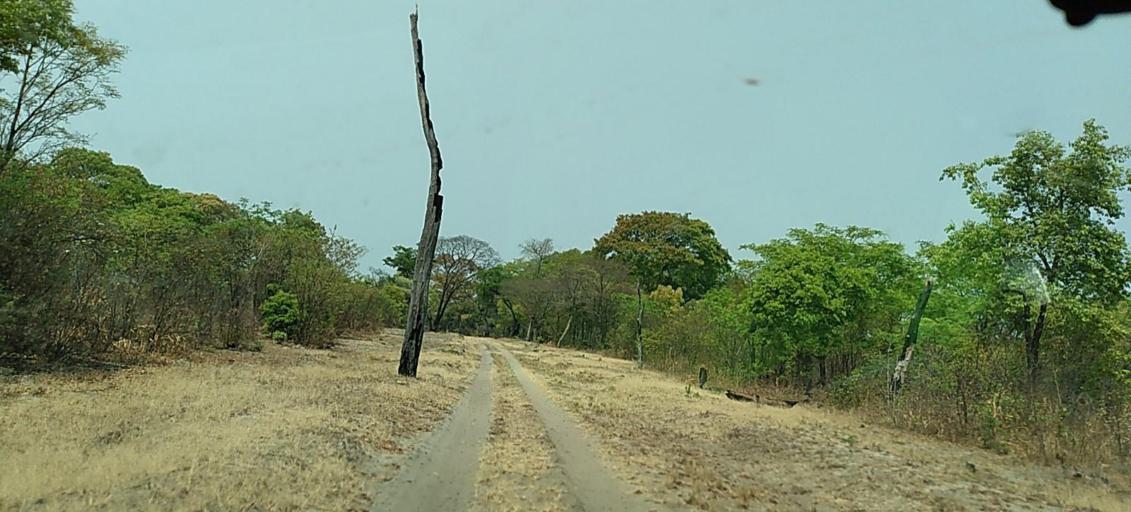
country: ZM
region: North-Western
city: Zambezi
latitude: -13.9272
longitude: 23.2257
